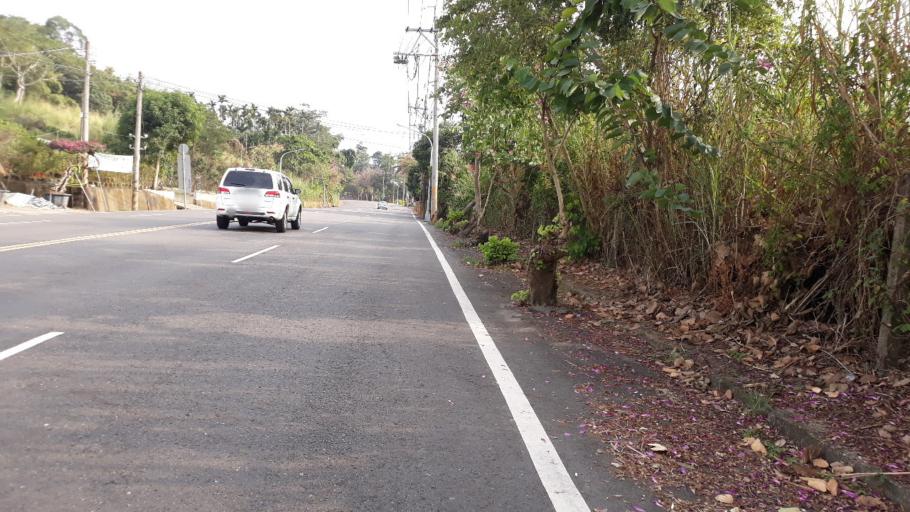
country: TW
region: Taiwan
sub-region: Chiayi
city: Jiayi Shi
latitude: 23.4274
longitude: 120.5173
